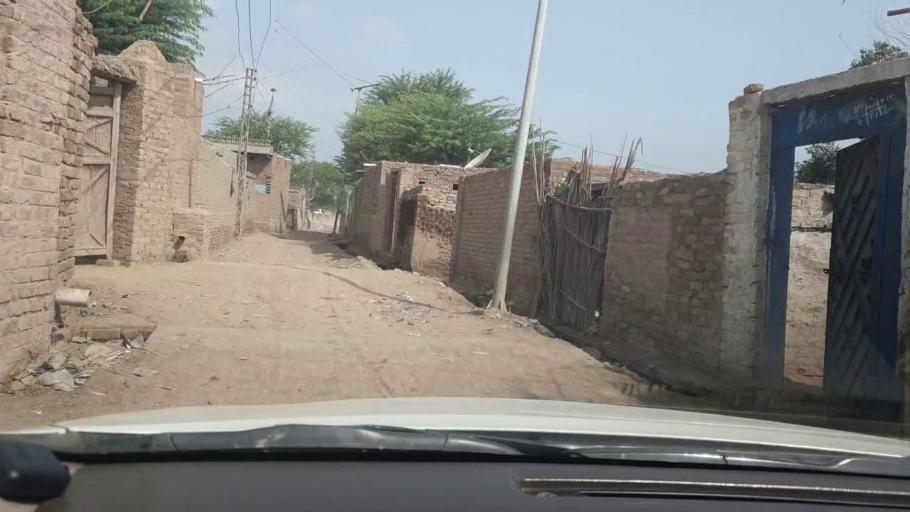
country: PK
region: Sindh
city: Shikarpur
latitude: 28.0070
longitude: 68.5929
